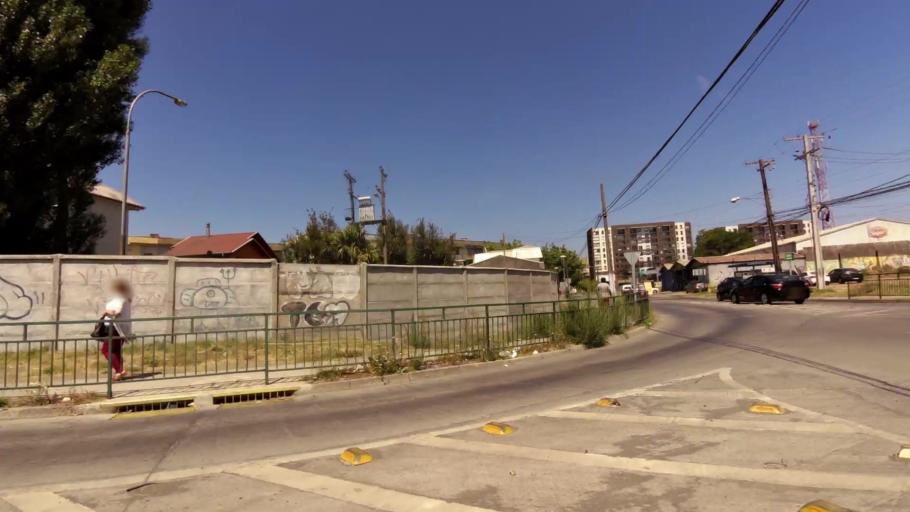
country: CL
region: Biobio
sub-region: Provincia de Concepcion
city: Concepcion
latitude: -36.8108
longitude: -73.0597
